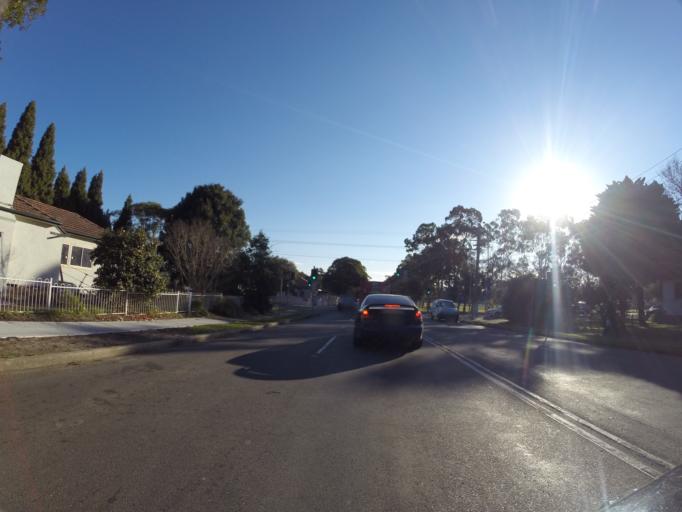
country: AU
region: New South Wales
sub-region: Auburn
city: Berala
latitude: -33.8638
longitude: 151.0189
